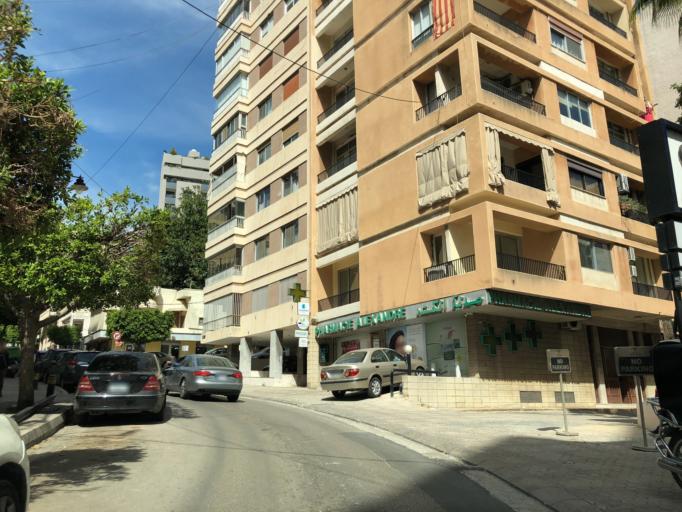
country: LB
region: Beyrouth
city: Beirut
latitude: 33.8834
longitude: 35.5190
